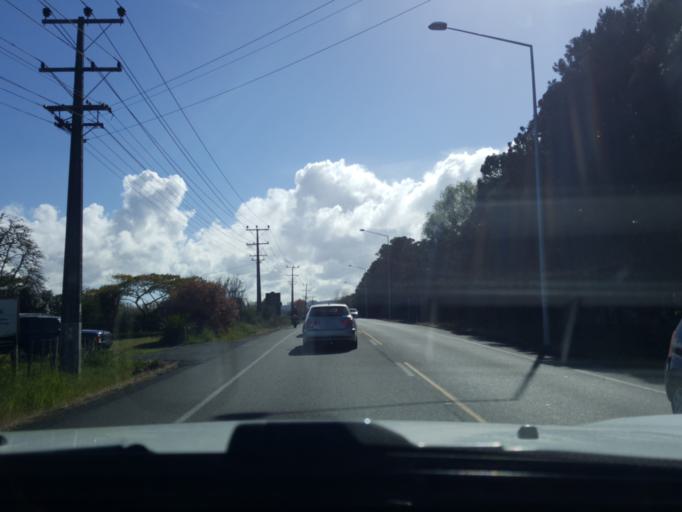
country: NZ
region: Auckland
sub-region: Auckland
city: Muriwai Beach
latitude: -36.7857
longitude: 174.5722
